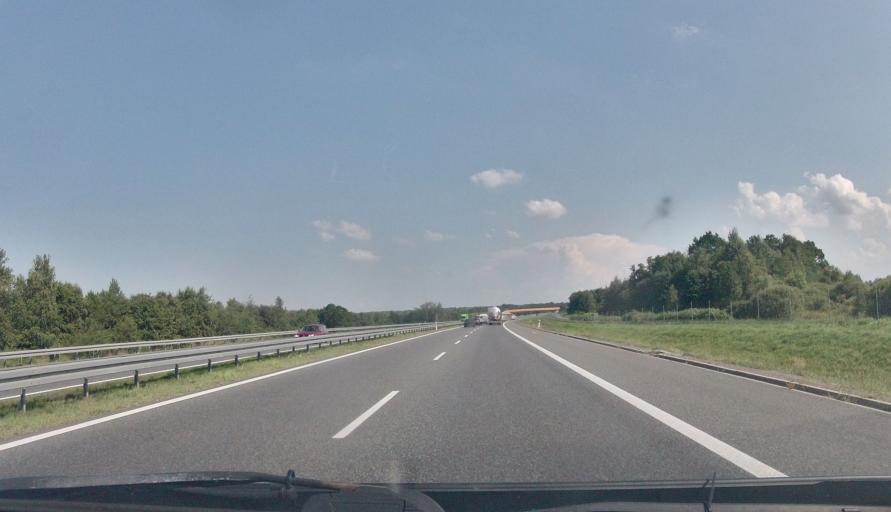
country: PL
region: Lesser Poland Voivodeship
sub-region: Powiat bochenski
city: Borek
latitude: 50.0084
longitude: 20.5279
